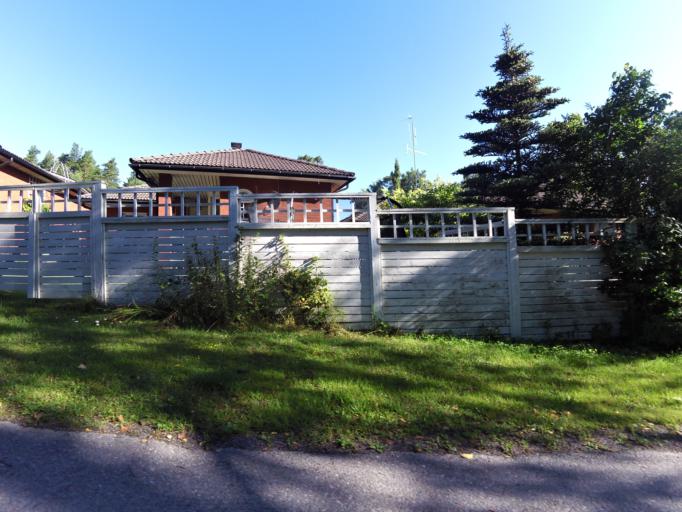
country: FI
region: Uusimaa
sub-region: Helsinki
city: Espoo
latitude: 60.1523
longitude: 24.6936
